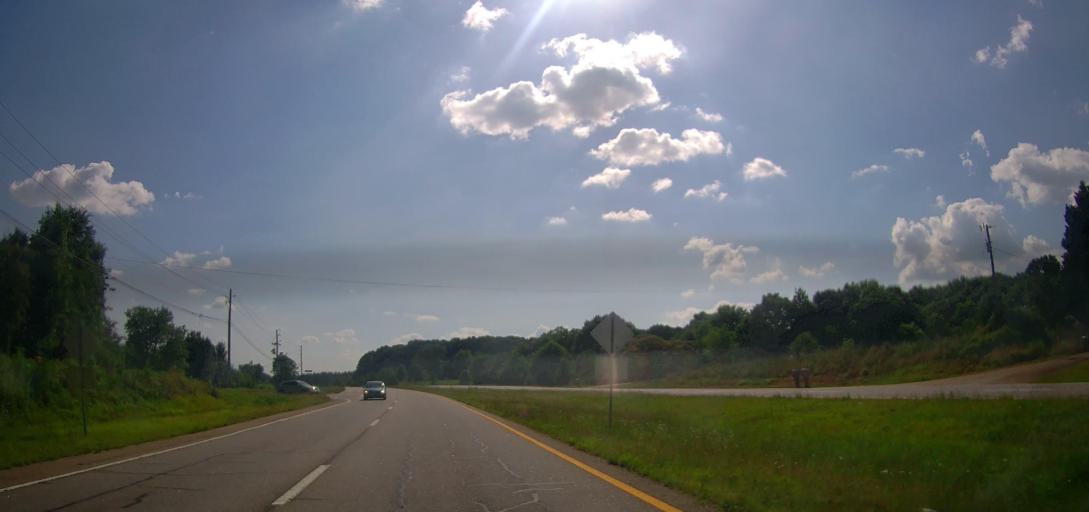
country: US
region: Georgia
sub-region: Henry County
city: Hampton
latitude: 33.4018
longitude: -84.2337
